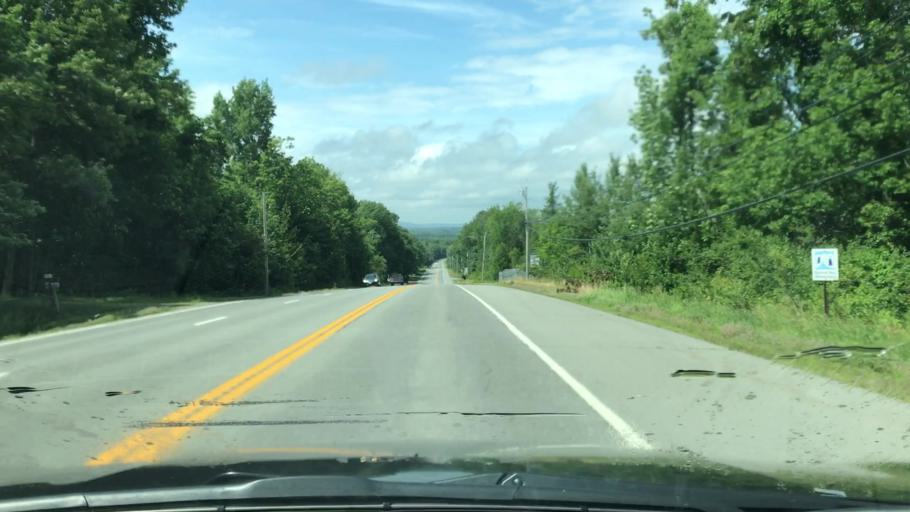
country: US
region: Maine
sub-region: Waldo County
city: Northport
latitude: 44.3617
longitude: -68.9760
